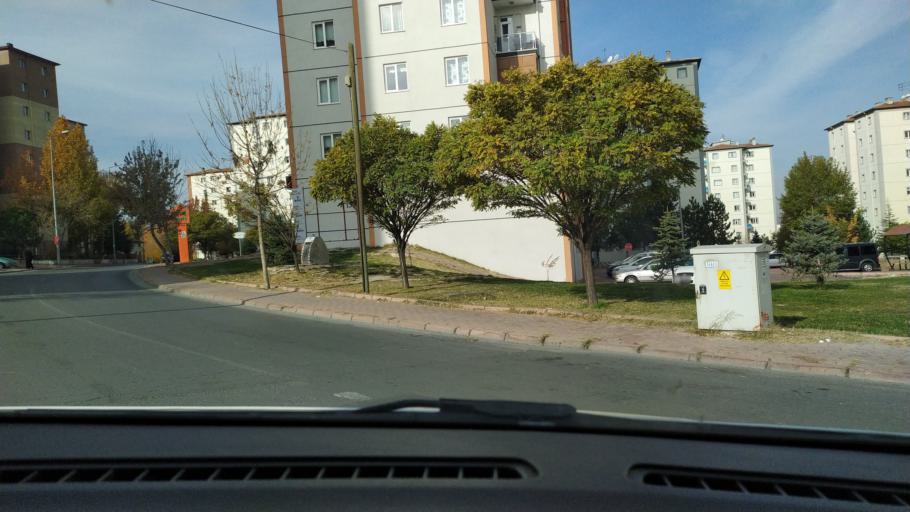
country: TR
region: Kayseri
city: Melikgazi
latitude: 38.7370
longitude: 35.3923
